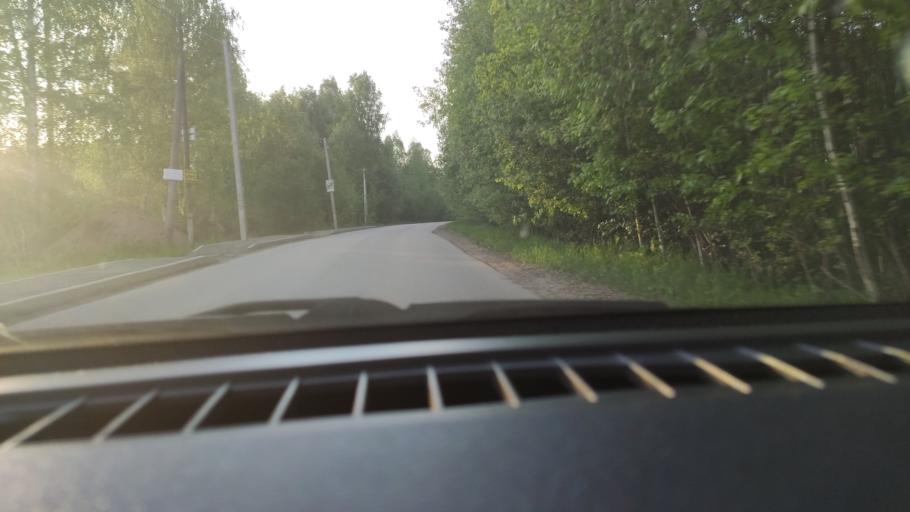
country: RU
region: Perm
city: Kondratovo
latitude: 58.0598
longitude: 56.0046
